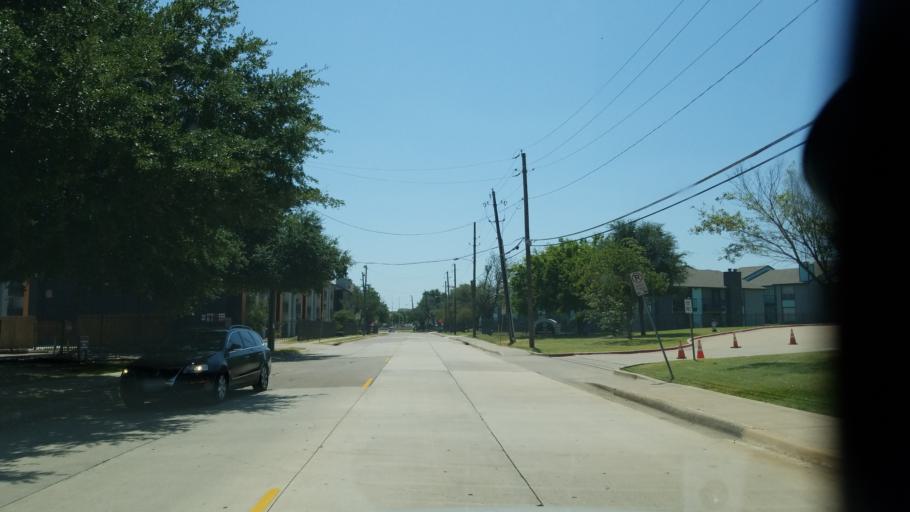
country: US
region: Texas
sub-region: Dallas County
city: Duncanville
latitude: 32.6535
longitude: -96.8833
